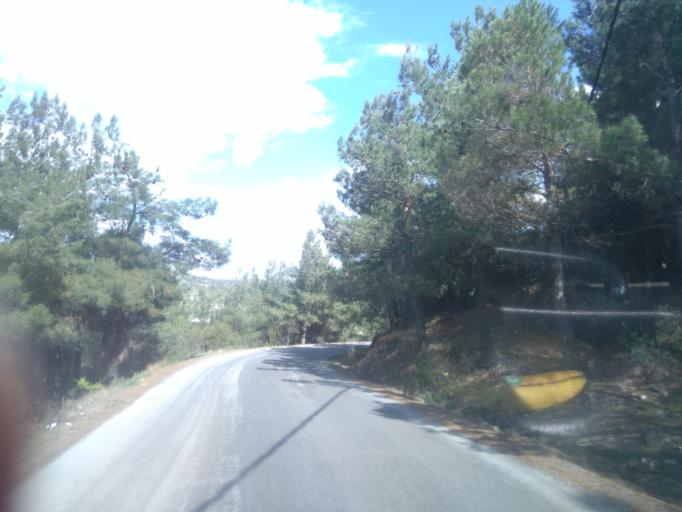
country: GR
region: Central Macedonia
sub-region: Nomos Thessalonikis
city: Asvestochori
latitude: 40.6399
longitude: 23.0119
